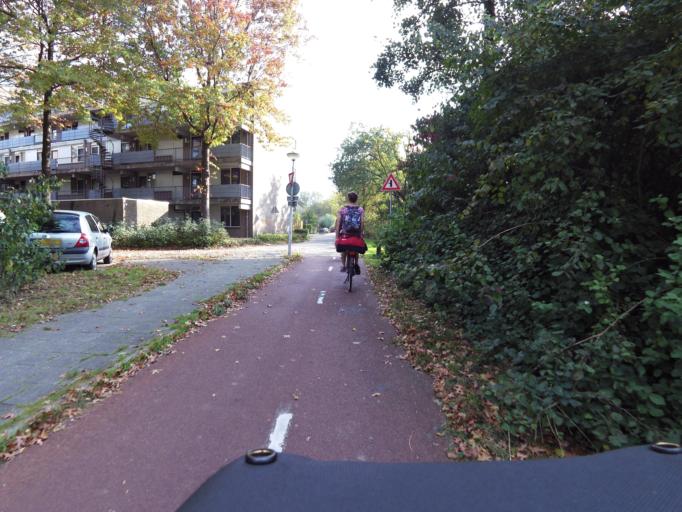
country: NL
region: Gelderland
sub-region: Gemeente Wageningen
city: Wageningen
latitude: 51.9773
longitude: 5.6494
